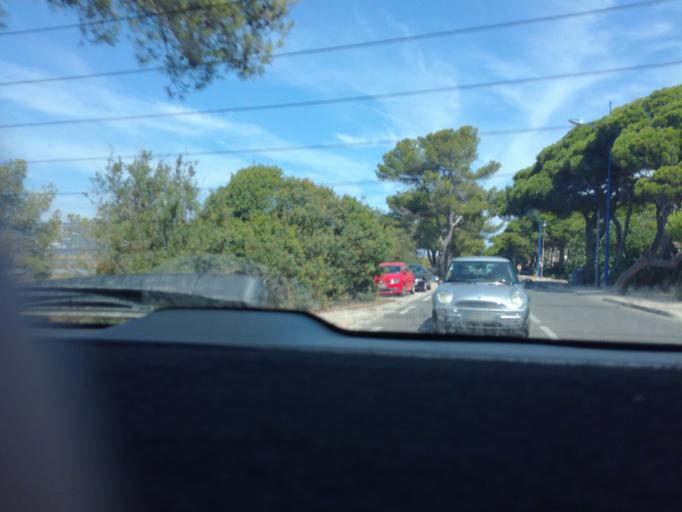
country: FR
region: Provence-Alpes-Cote d'Azur
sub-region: Departement du Var
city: Hyeres
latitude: 43.0618
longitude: 6.1472
